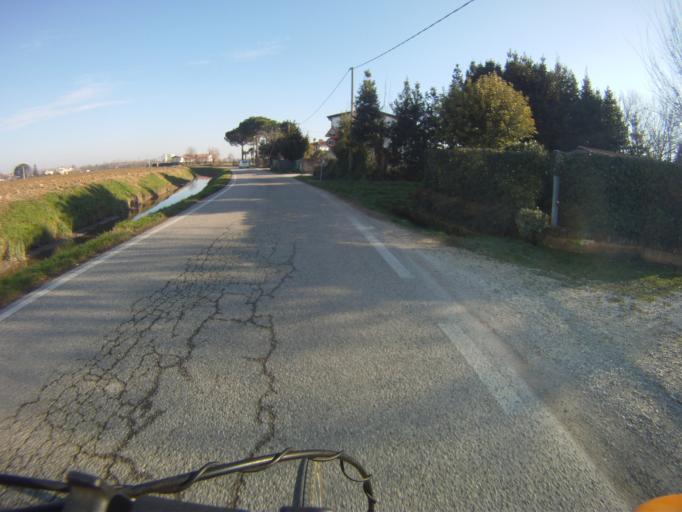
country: IT
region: Veneto
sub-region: Provincia di Padova
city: Piove di Sacco-Piovega
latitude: 45.2926
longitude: 12.0173
